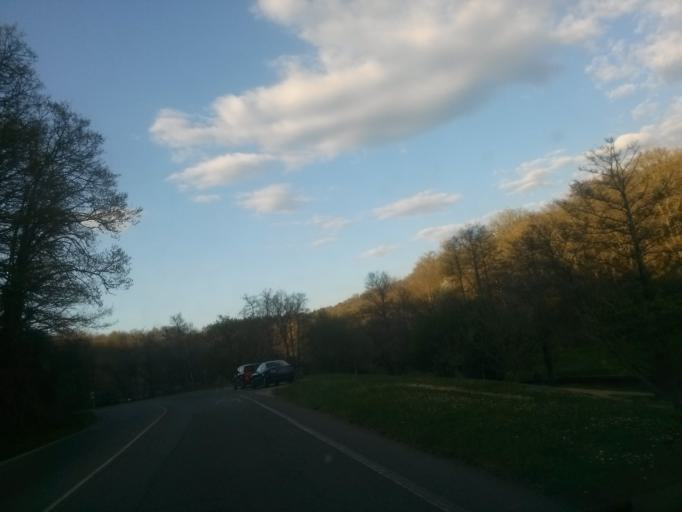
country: ES
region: Galicia
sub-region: Provincia de Lugo
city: Lugo
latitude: 42.9952
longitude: -7.5343
